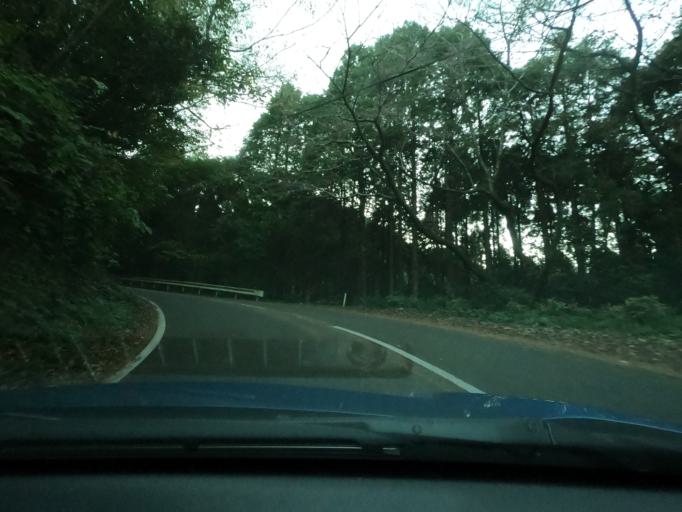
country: JP
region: Kagoshima
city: Satsumasendai
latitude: 31.8198
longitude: 130.4785
